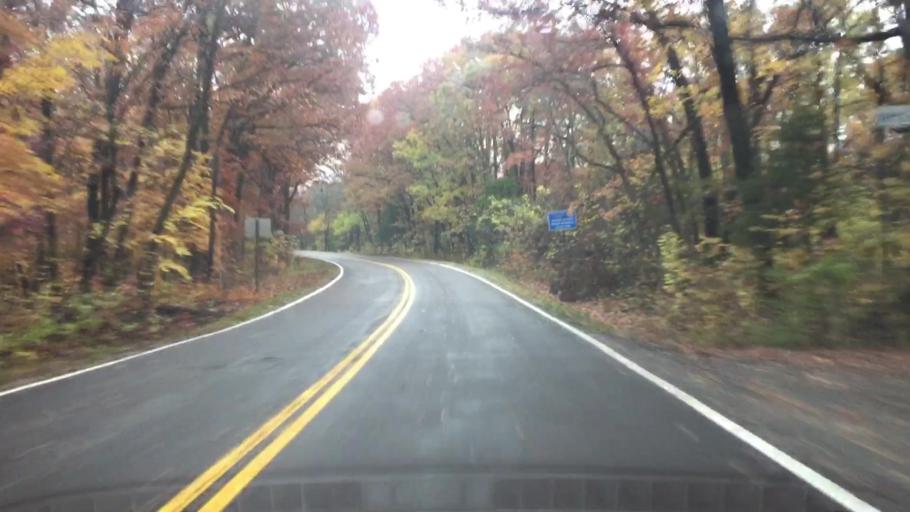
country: US
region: Missouri
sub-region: Boone County
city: Columbia
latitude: 38.8686
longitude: -92.3183
